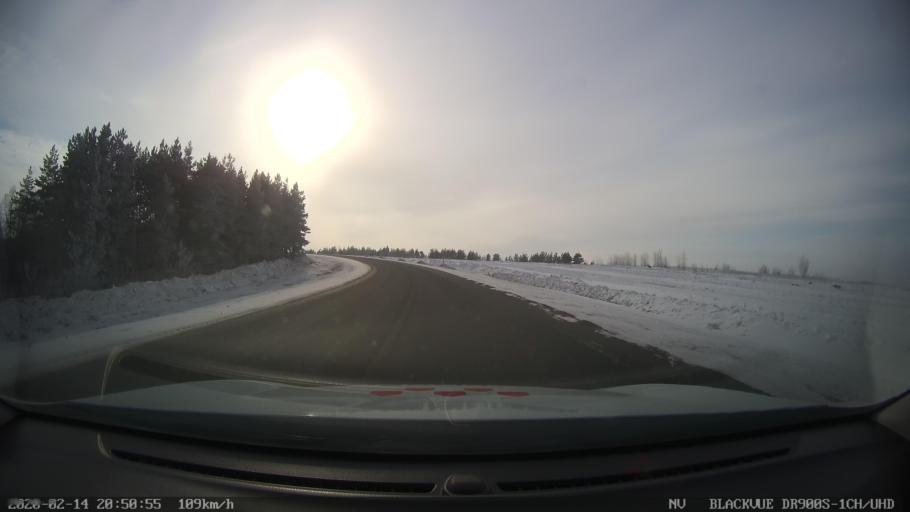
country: RU
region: Tatarstan
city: Kuybyshevskiy Zaton
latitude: 55.2193
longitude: 49.2321
